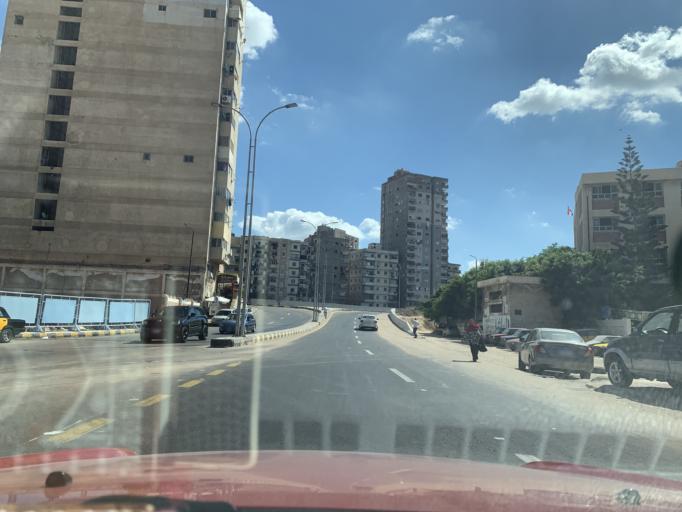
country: EG
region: Alexandria
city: Alexandria
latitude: 31.2149
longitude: 29.9611
